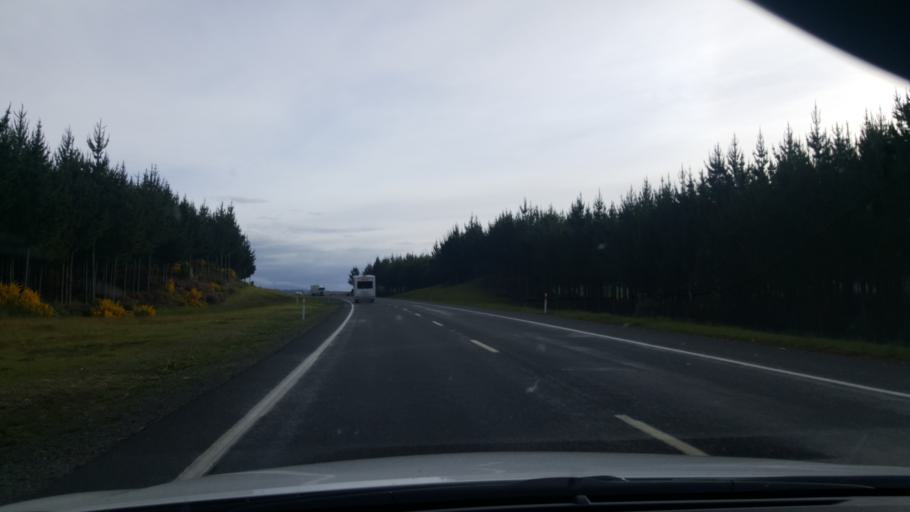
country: NZ
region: Waikato
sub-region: Taupo District
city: Taupo
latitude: -38.8267
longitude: 176.0679
